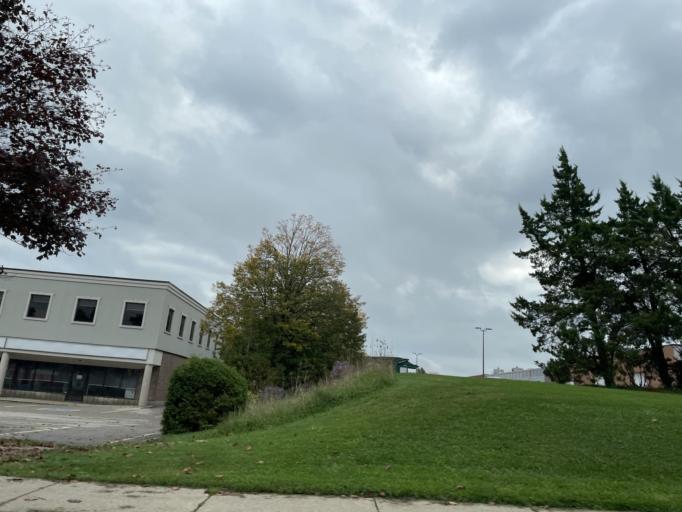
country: CA
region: Ontario
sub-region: Wellington County
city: Guelph
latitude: 43.5396
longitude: -80.2940
